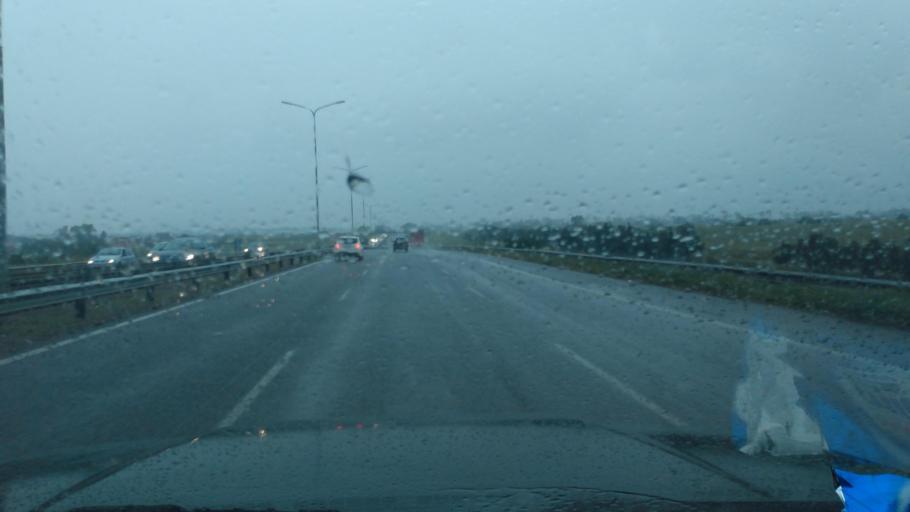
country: AR
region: Buenos Aires
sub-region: Partido de Tigre
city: Tigre
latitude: -34.5104
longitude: -58.5902
